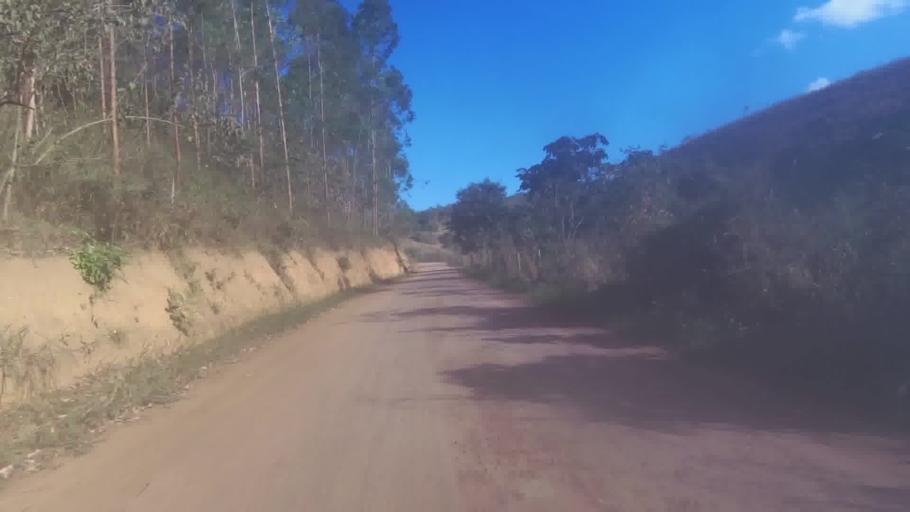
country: BR
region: Espirito Santo
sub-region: Mimoso Do Sul
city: Mimoso do Sul
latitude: -21.1008
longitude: -41.1373
